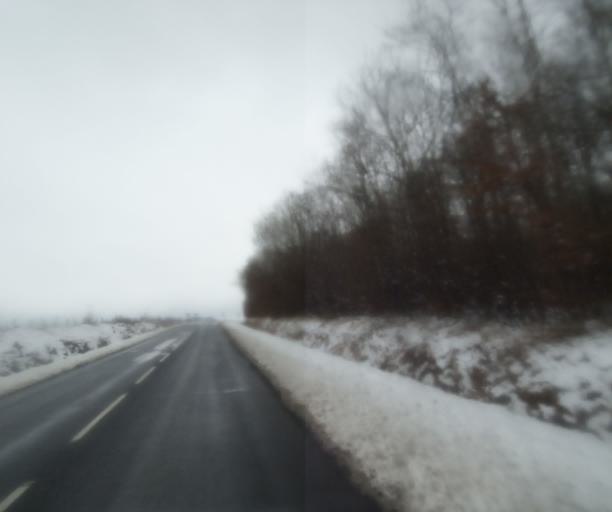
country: FR
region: Champagne-Ardenne
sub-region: Departement de la Haute-Marne
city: Laneuville-a-Remy
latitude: 48.4919
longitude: 4.8423
